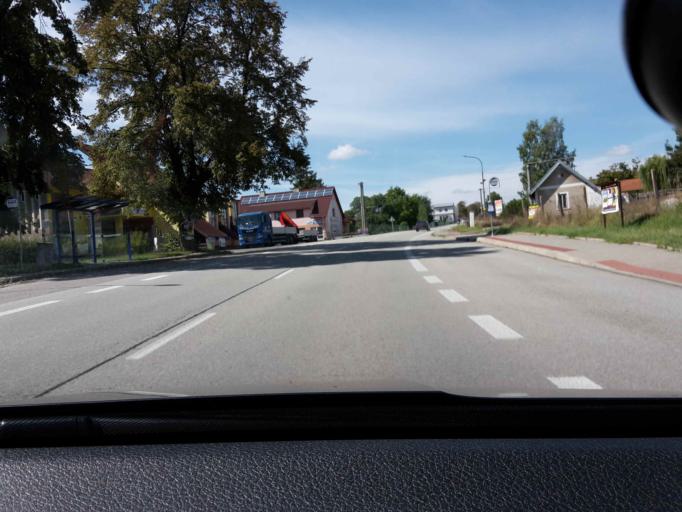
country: CZ
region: Jihocesky
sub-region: Okres Jindrichuv Hradec
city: Jindrichuv Hradec
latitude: 49.1592
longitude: 14.9563
